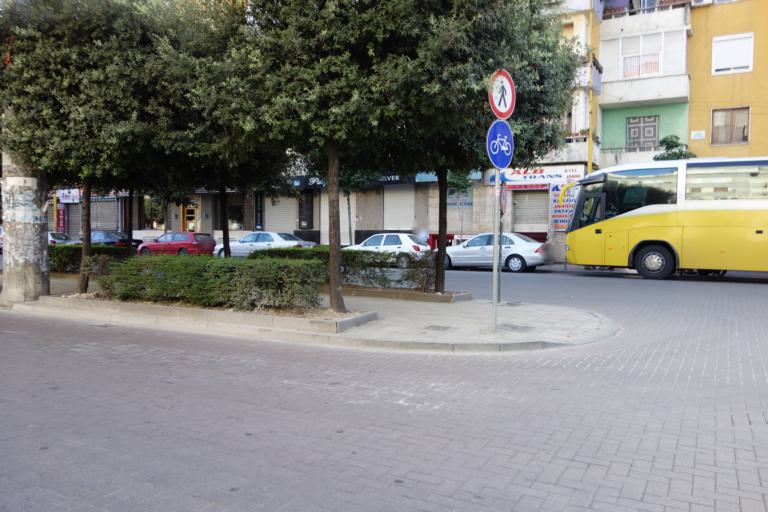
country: AL
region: Tirane
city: Tirana
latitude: 41.3333
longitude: 19.8169
